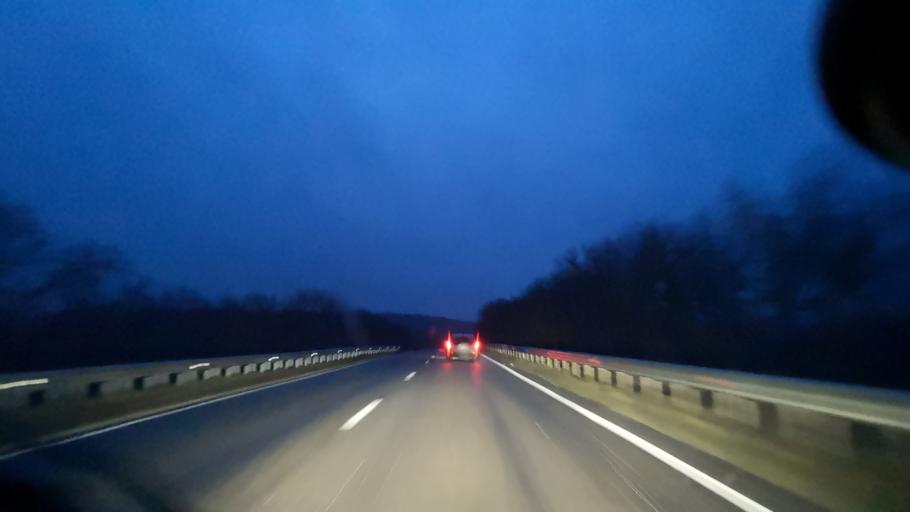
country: MD
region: Orhei
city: Orhei
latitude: 47.4921
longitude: 28.7918
